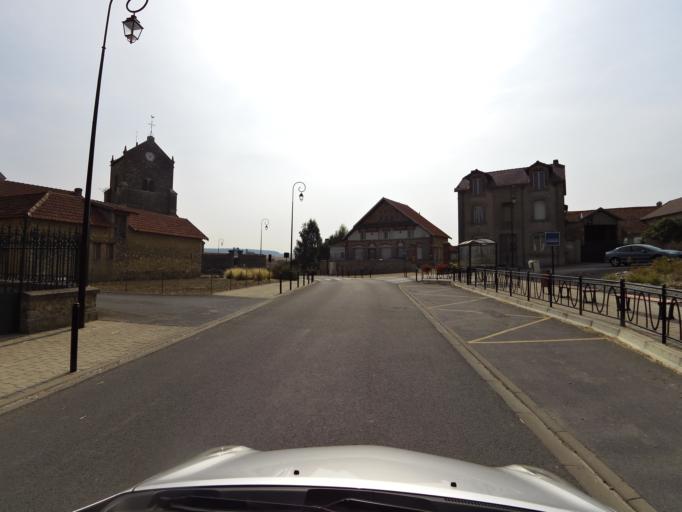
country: FR
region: Champagne-Ardenne
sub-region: Departement de la Marne
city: Gueux
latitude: 49.1749
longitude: 3.8647
